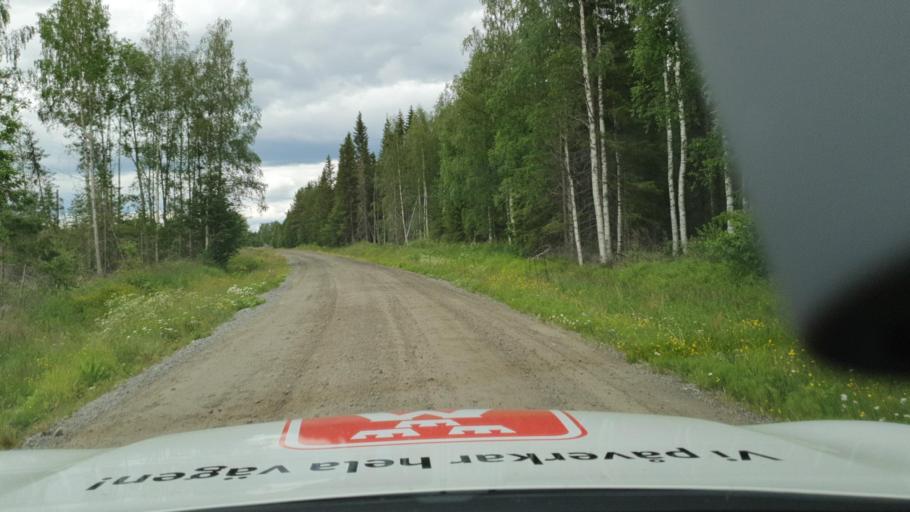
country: SE
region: Vaesterbotten
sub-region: Bjurholms Kommun
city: Bjurholm
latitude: 63.7884
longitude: 19.1099
